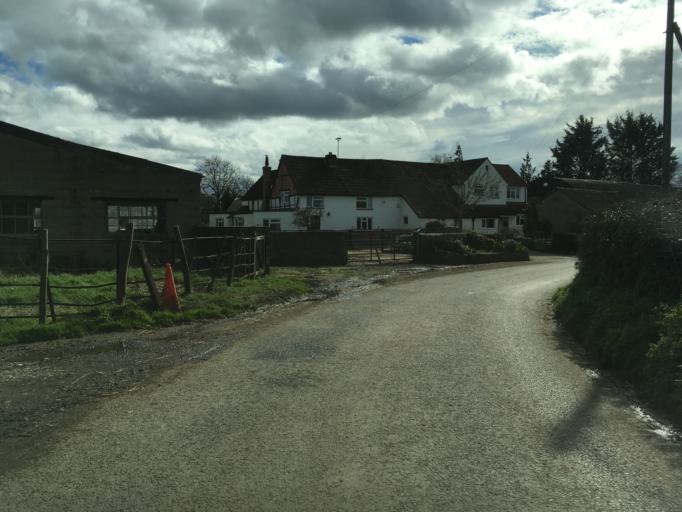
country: GB
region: England
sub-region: Gloucestershire
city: Newent
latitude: 51.8622
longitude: -2.3788
